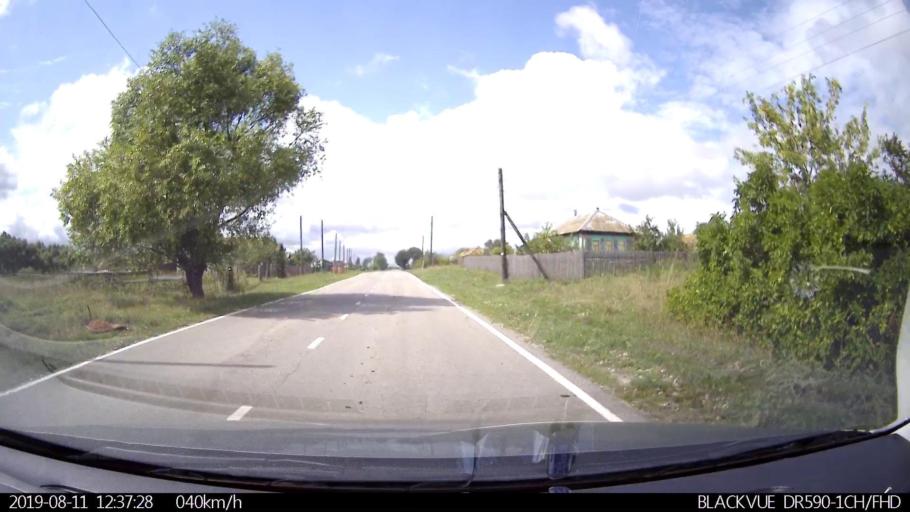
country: RU
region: Ulyanovsk
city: Ignatovka
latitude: 53.8240
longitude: 47.8148
